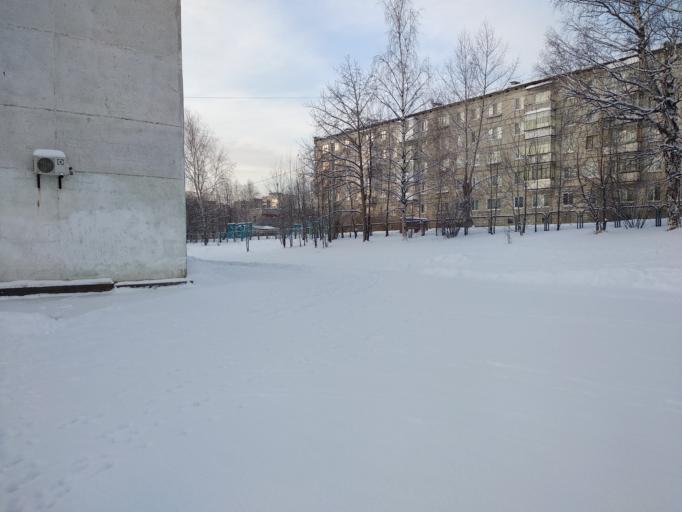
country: RU
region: Sverdlovsk
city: Krasnotur'insk
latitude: 59.7651
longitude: 60.2145
